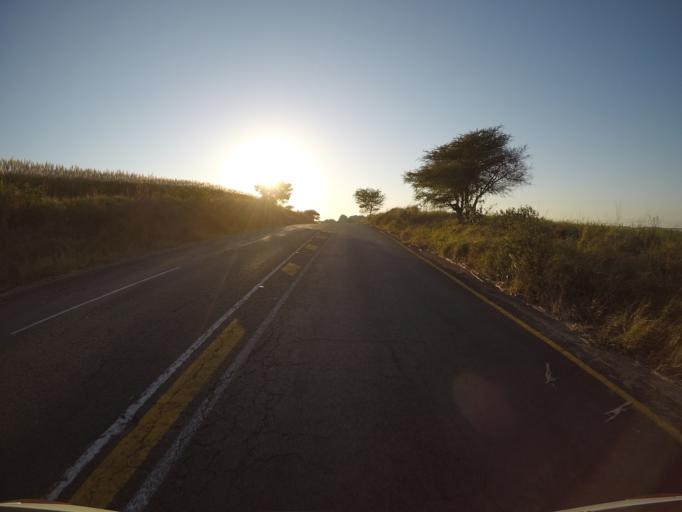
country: ZA
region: KwaZulu-Natal
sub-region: uThungulu District Municipality
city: Eshowe
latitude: -28.9497
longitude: 31.6740
